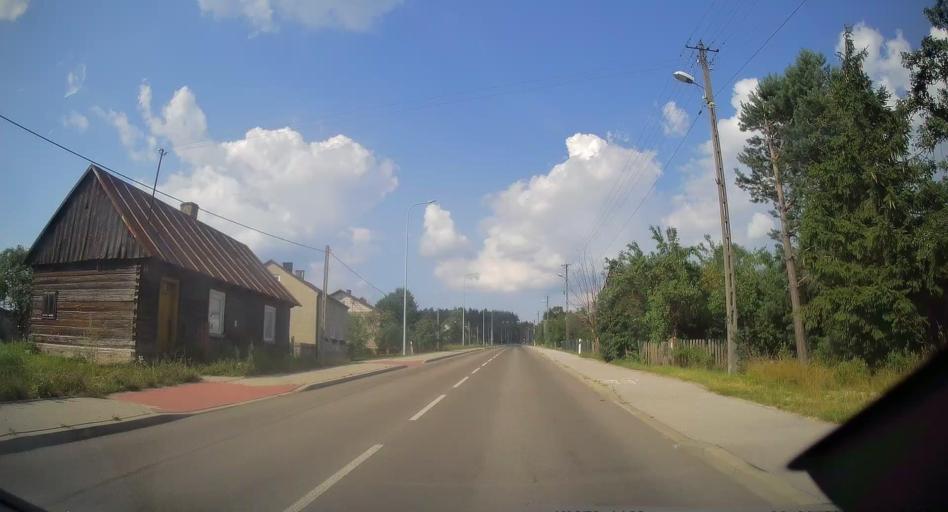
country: PL
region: Swietokrzyskie
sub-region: Powiat konecki
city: Radoszyce
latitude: 51.0138
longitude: 20.2865
